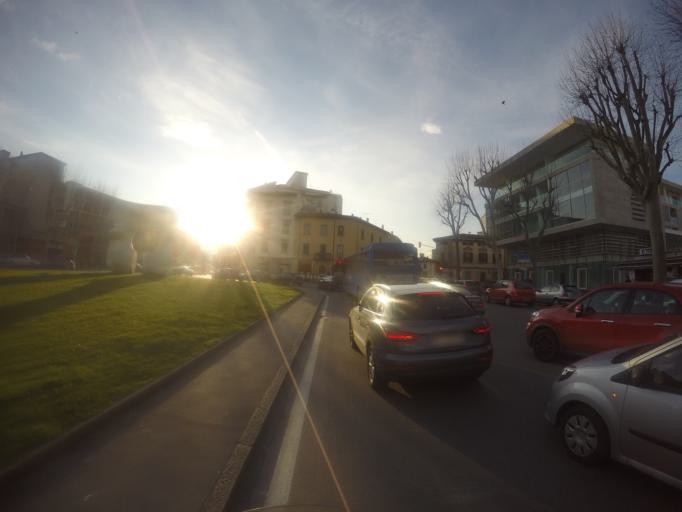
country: IT
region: Tuscany
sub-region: Provincia di Prato
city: Prato
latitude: 43.8779
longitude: 11.1013
